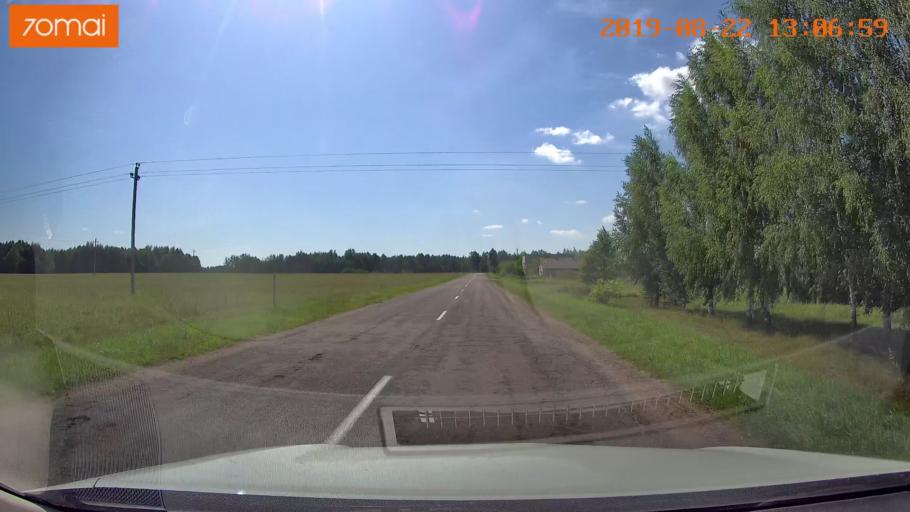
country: BY
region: Minsk
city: Prawdzinski
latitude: 53.3404
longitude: 27.8345
